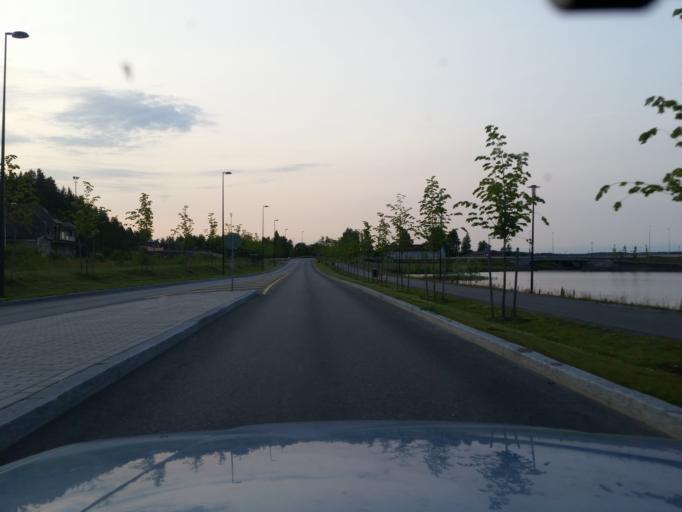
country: FI
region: Southern Savonia
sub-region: Savonlinna
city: Savonlinna
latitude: 61.8735
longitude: 28.8750
